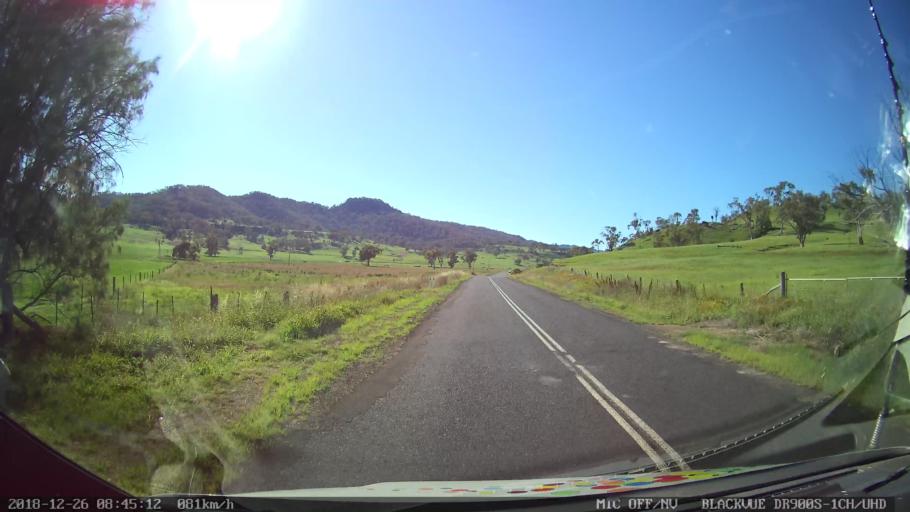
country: AU
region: New South Wales
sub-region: Mid-Western Regional
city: Kandos
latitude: -32.5227
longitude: 150.0849
